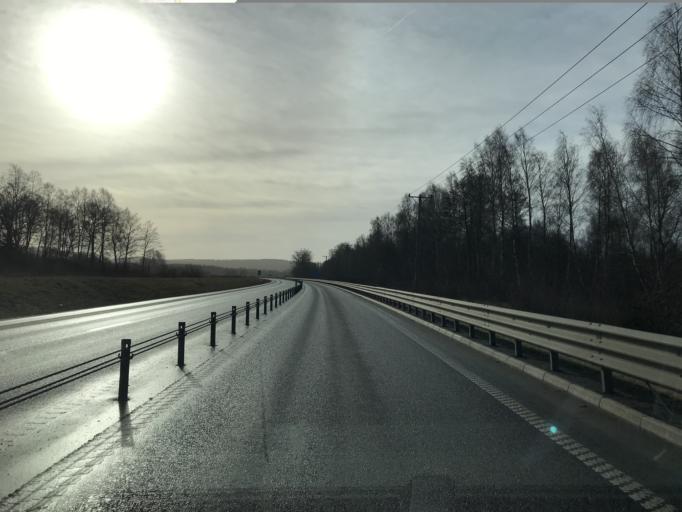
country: SE
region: Skane
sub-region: Hassleholms Kommun
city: Hassleholm
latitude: 56.1428
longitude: 13.8185
